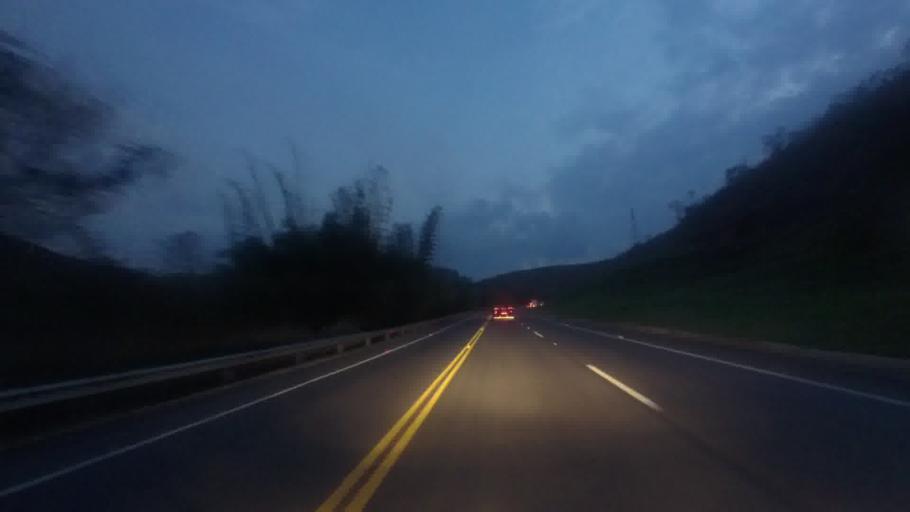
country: BR
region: Rio de Janeiro
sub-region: Sapucaia
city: Sapucaia
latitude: -21.9511
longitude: -42.8399
